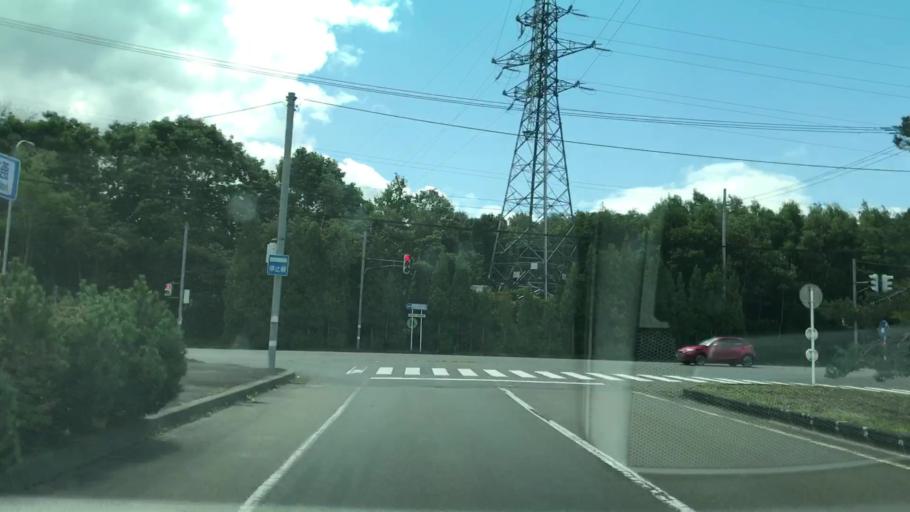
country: JP
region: Hokkaido
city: Chitose
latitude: 42.7729
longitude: 141.6167
